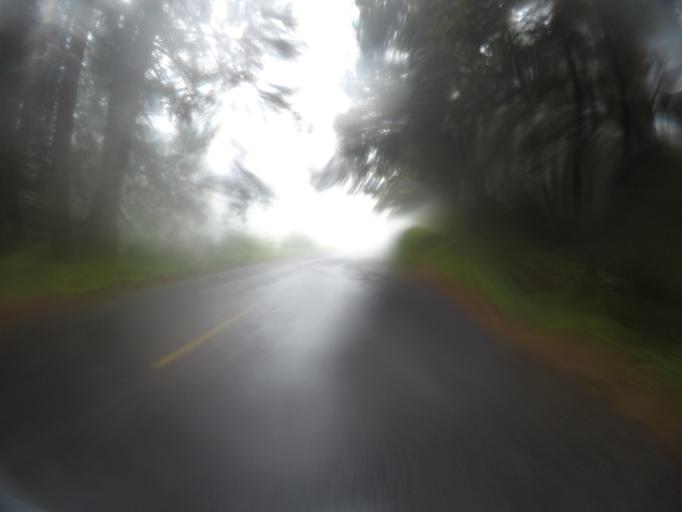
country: US
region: California
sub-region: Humboldt County
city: Westhaven-Moonstone
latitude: 41.2748
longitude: -124.0030
